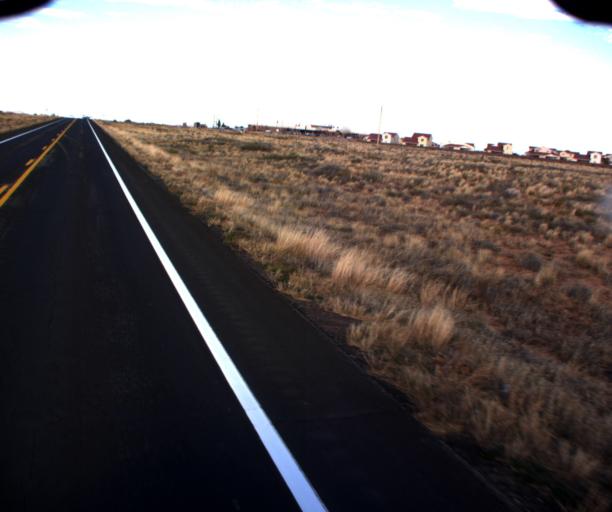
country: US
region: Arizona
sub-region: Apache County
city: Lukachukai
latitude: 36.9595
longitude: -109.3428
